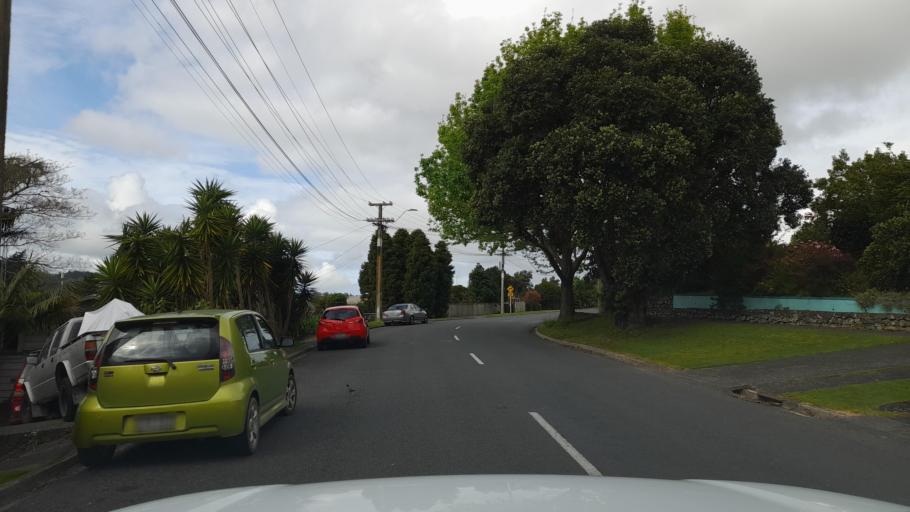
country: NZ
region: Northland
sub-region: Whangarei
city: Whangarei
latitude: -35.7358
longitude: 174.3257
